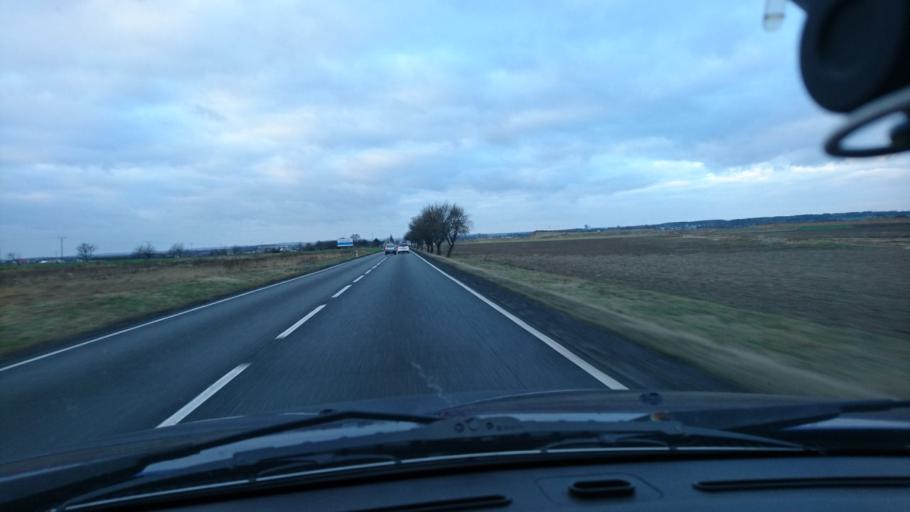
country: PL
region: Greater Poland Voivodeship
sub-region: Powiat kepinski
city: Baranow
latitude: 51.2504
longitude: 18.0152
